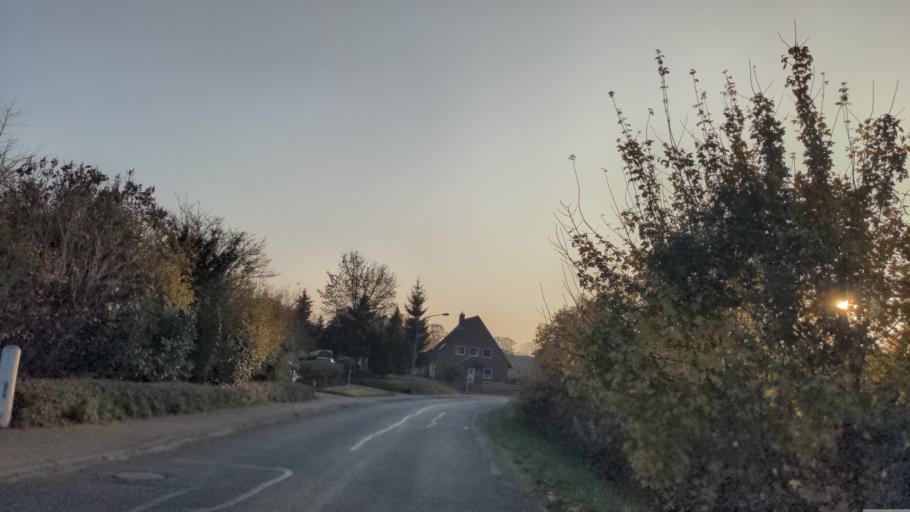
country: DE
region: Schleswig-Holstein
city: Bosdorf
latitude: 54.1321
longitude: 10.5044
